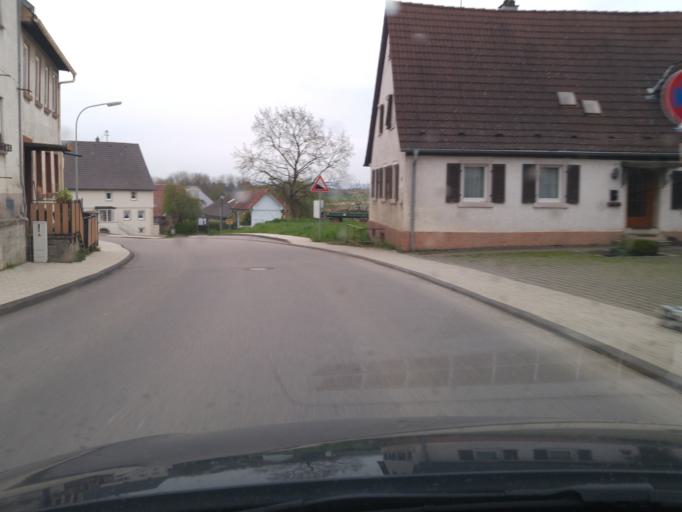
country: DE
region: Baden-Wuerttemberg
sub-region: Regierungsbezirk Stuttgart
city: Offenau
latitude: 49.2433
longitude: 9.1371
